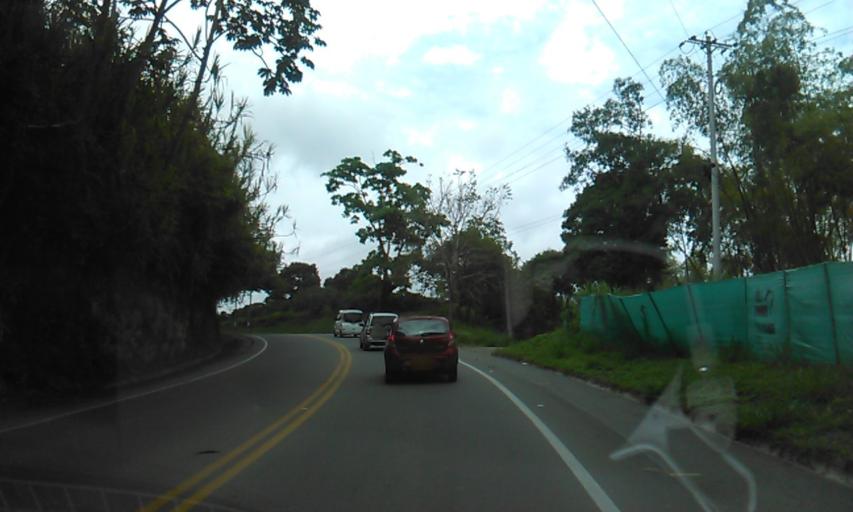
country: CO
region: Quindio
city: Montenegro
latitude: 4.5436
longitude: -75.7414
